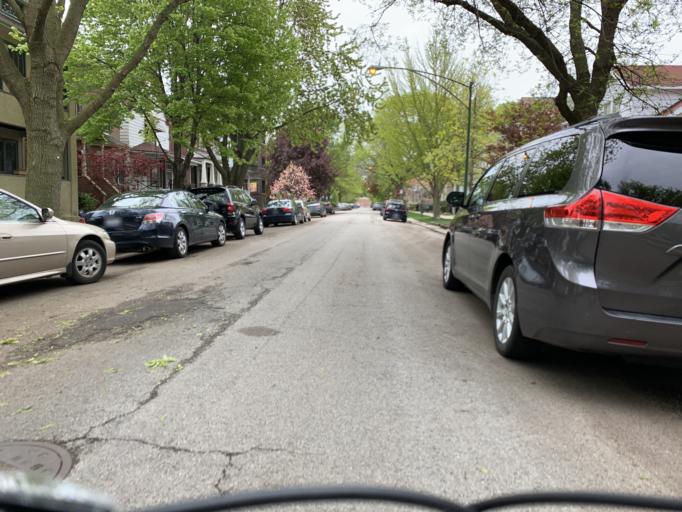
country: US
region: Illinois
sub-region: Cook County
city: Lincolnwood
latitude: 41.9713
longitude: -87.6831
